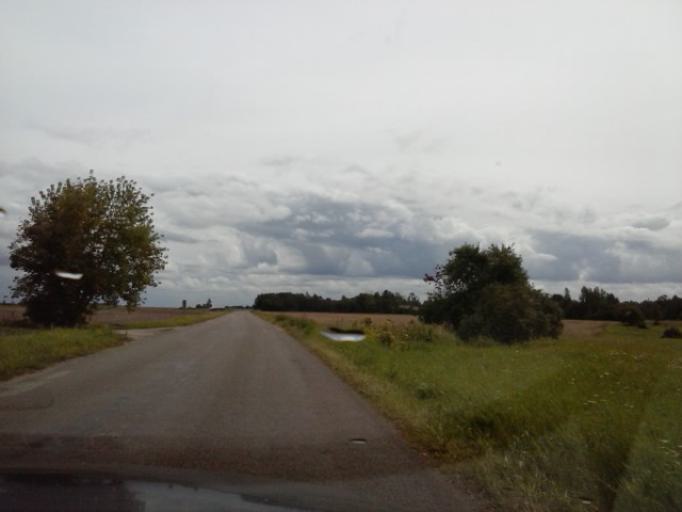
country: LV
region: Tukuma Rajons
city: Tukums
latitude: 56.8916
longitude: 23.2361
